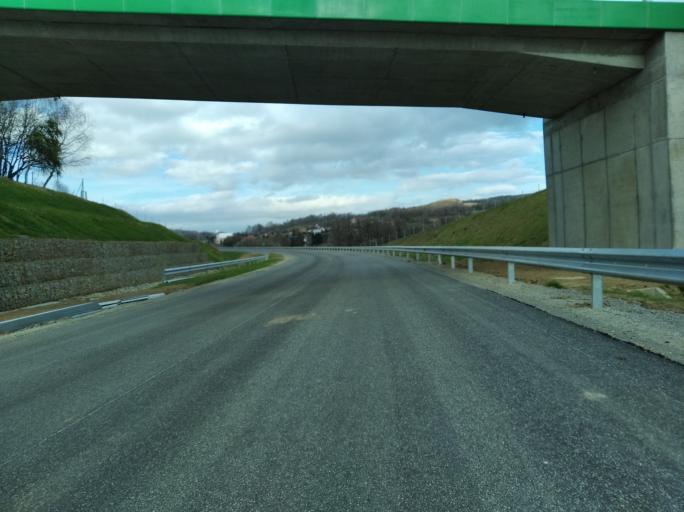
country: PL
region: Subcarpathian Voivodeship
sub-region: Powiat strzyzowski
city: Strzyzow
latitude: 49.8656
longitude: 21.8200
